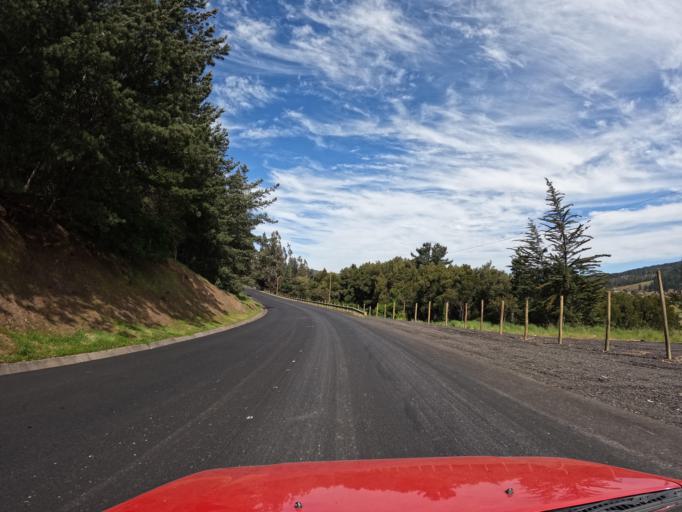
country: CL
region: Maule
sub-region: Provincia de Talca
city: Constitucion
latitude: -35.0435
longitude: -72.0591
